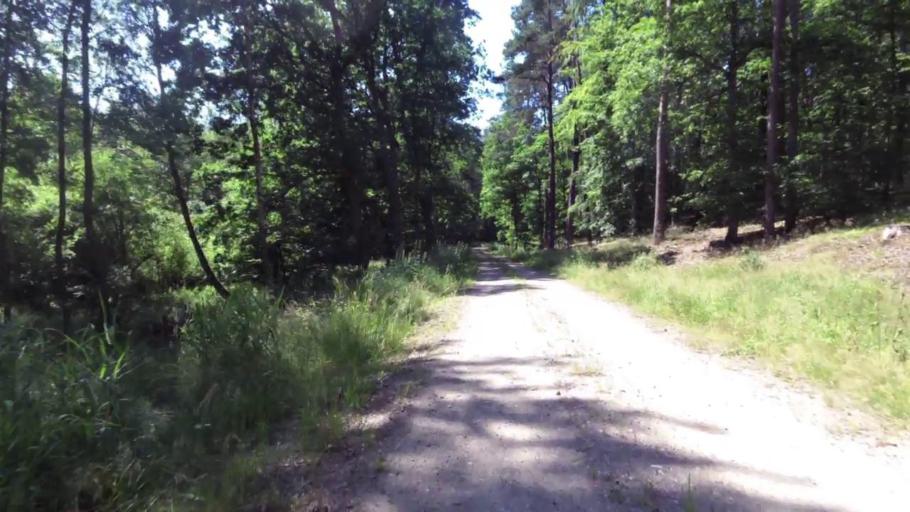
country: PL
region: West Pomeranian Voivodeship
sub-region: Powiat swidwinski
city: Polczyn-Zdroj
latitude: 53.8040
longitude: 16.1196
